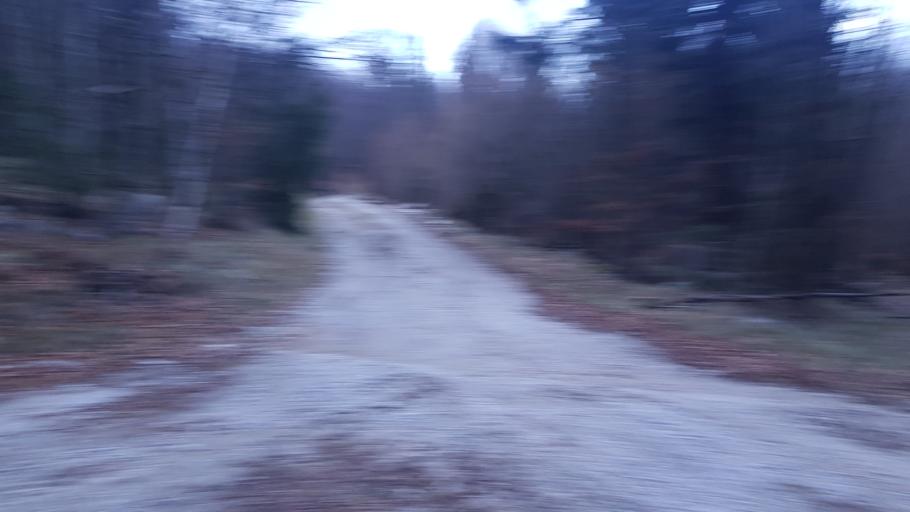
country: SI
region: Kanal
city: Kanal
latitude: 46.0452
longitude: 13.7321
